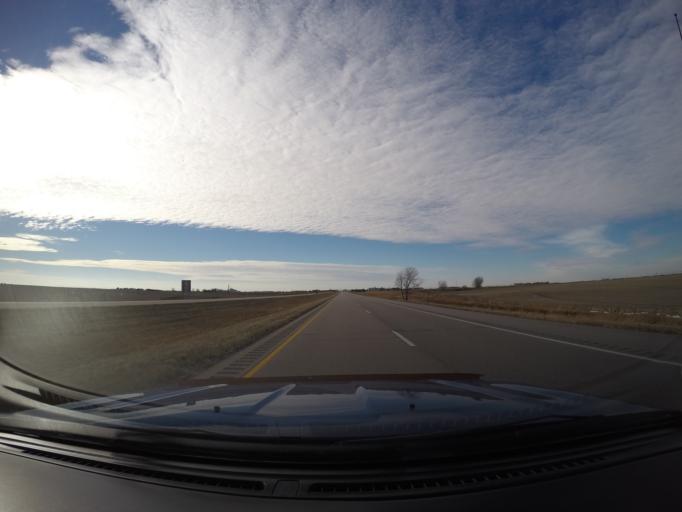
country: US
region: Nebraska
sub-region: Hamilton County
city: Aurora
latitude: 40.8212
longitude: -97.9068
